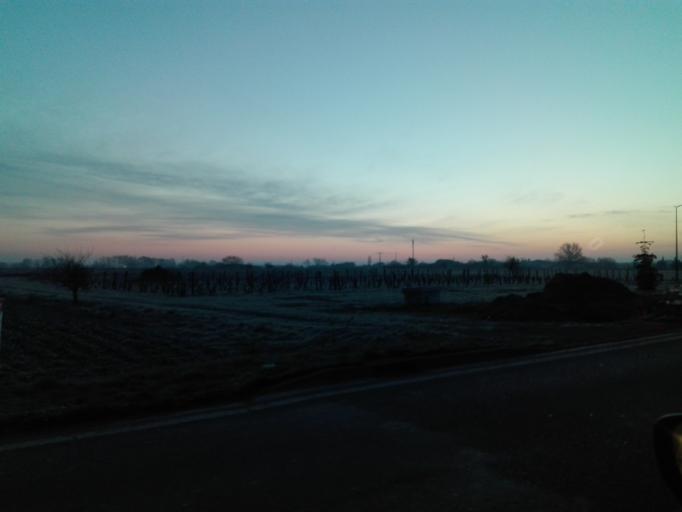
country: FR
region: Midi-Pyrenees
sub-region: Departement de la Haute-Garonne
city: Seilh
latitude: 43.6988
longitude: 1.3483
